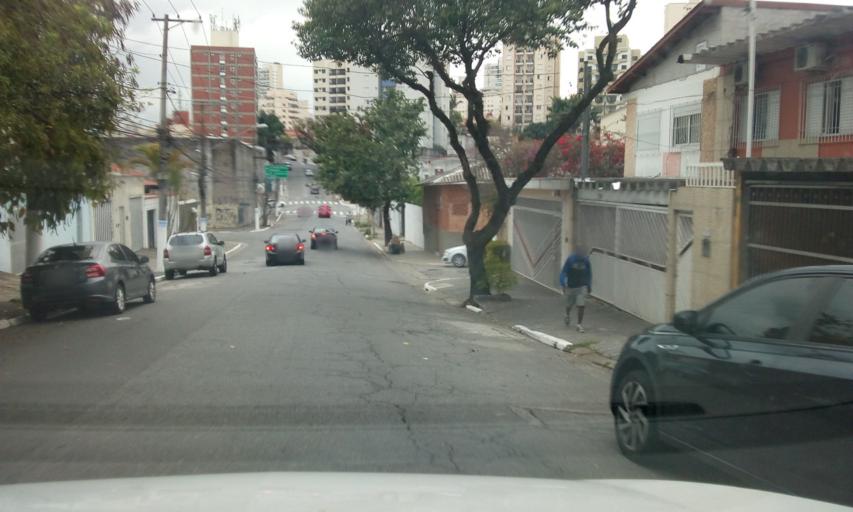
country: BR
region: Sao Paulo
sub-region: Sao Paulo
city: Sao Paulo
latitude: -23.6169
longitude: -46.6446
